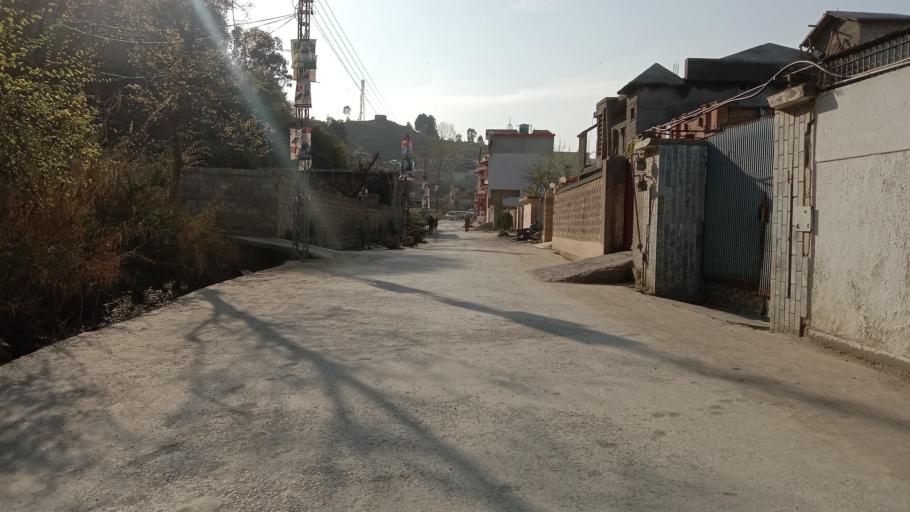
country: PK
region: Khyber Pakhtunkhwa
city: Abbottabad
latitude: 34.2031
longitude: 73.2233
